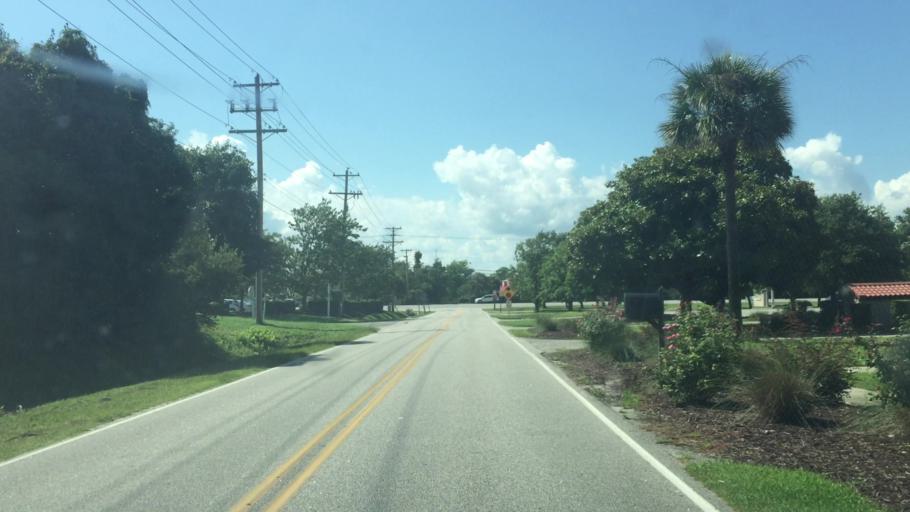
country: US
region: South Carolina
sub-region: Horry County
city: North Myrtle Beach
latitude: 33.8339
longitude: -78.6705
